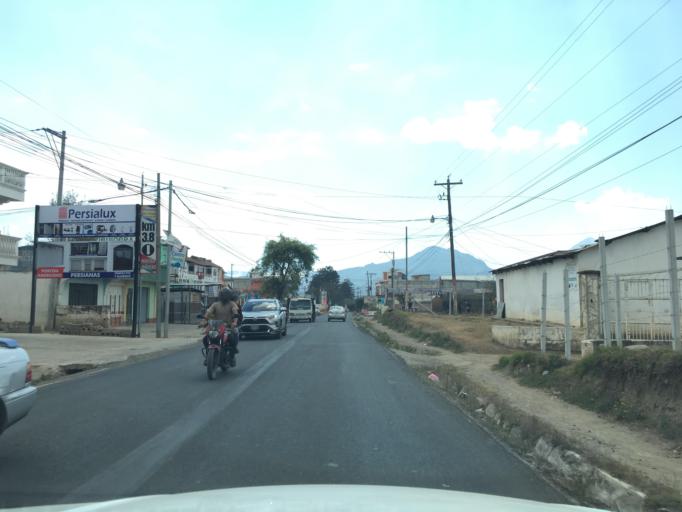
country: GT
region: Quetzaltenango
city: Olintepeque
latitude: 14.8740
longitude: -91.5135
